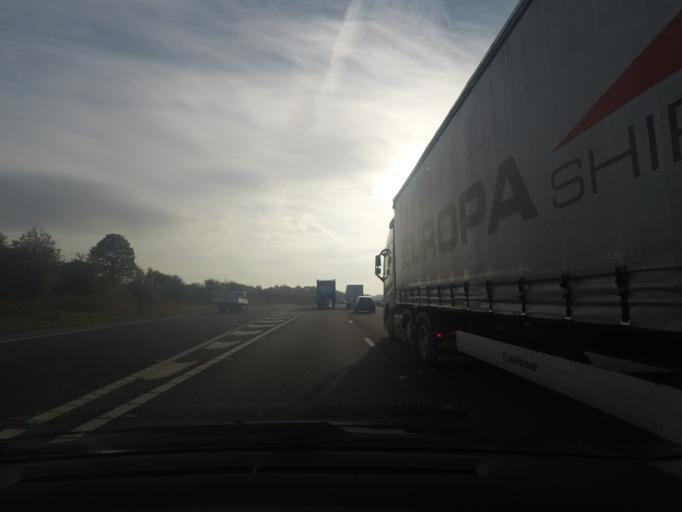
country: GB
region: England
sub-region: Barnsley
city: Dodworth
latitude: 53.5532
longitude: -1.5224
